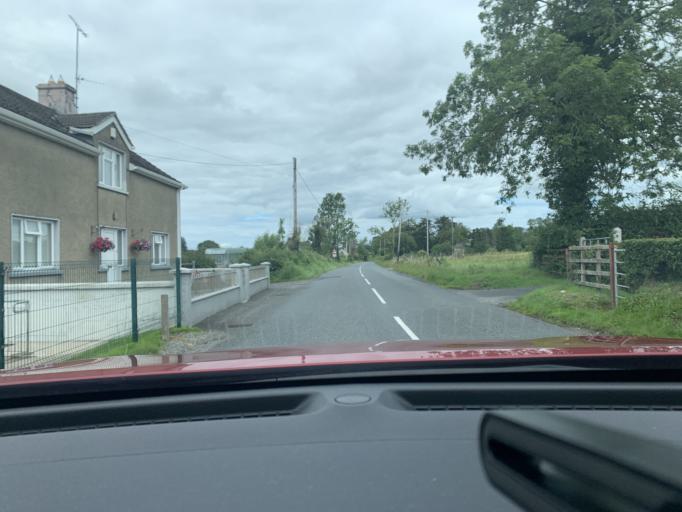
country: GB
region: Northern Ireland
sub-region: Fermanagh District
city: Enniskillen
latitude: 54.2786
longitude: -7.7025
